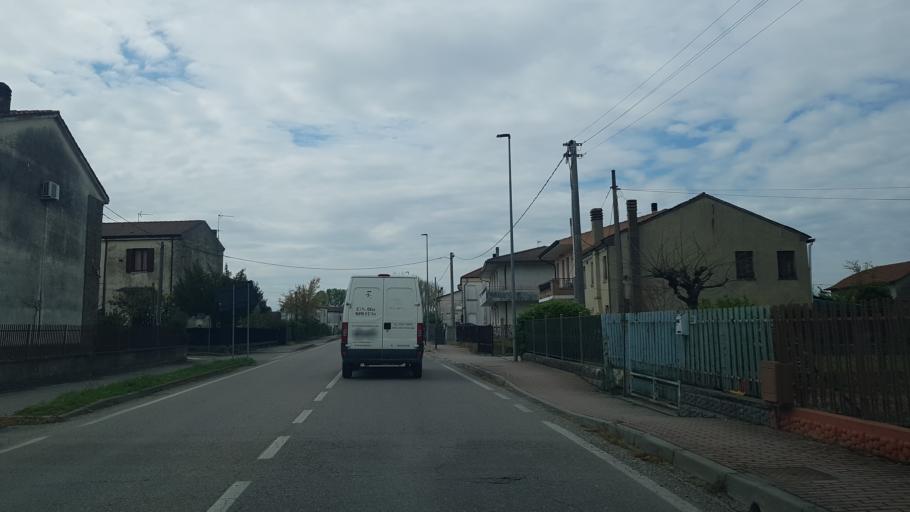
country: IT
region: Veneto
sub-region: Provincia di Padova
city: Piacenza d'Adige
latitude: 45.1267
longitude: 11.5446
